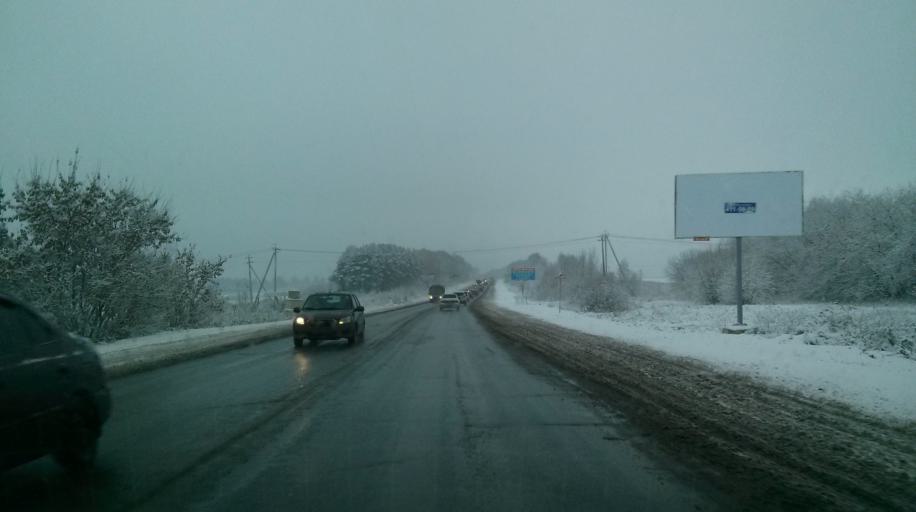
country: RU
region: Nizjnij Novgorod
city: Burevestnik
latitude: 56.1636
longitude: 43.7258
